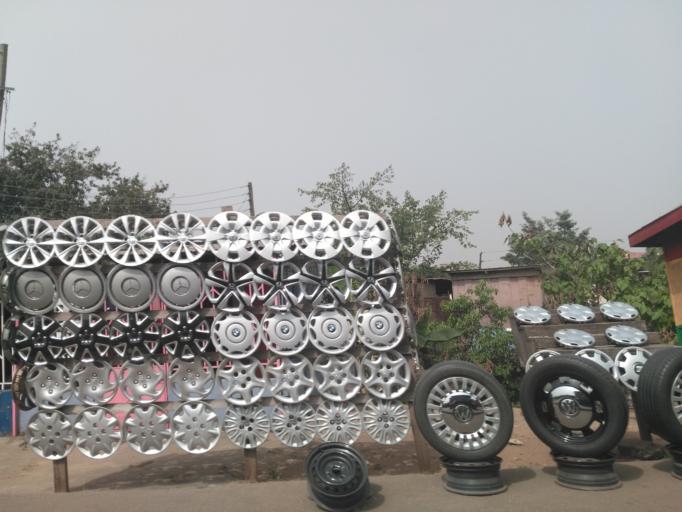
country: GH
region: Ashanti
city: Kumasi
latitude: 6.6862
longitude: -1.6072
